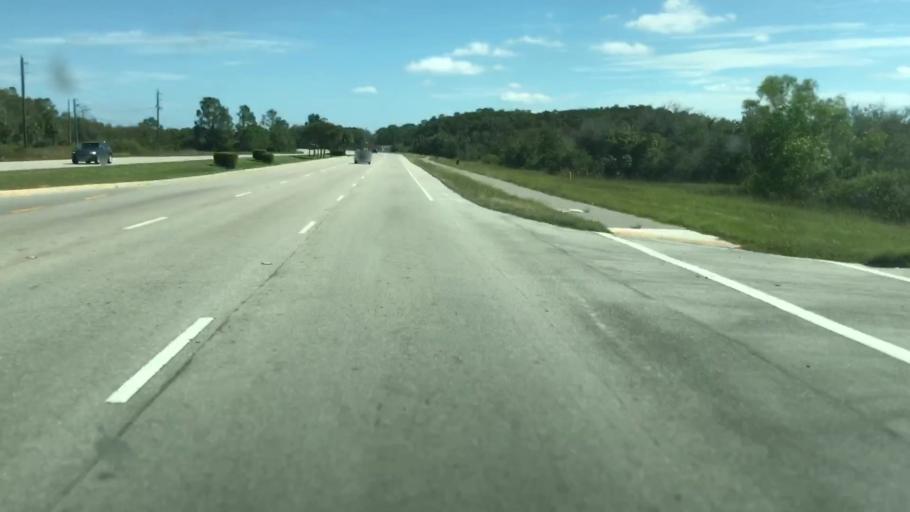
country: US
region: Florida
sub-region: Lee County
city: Gateway
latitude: 26.5476
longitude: -81.7678
